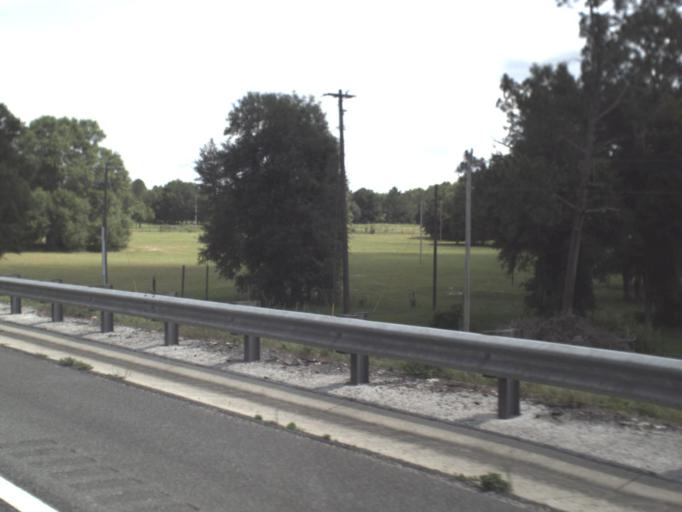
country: US
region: Florida
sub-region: Columbia County
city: Lake City
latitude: 30.1475
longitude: -82.6719
